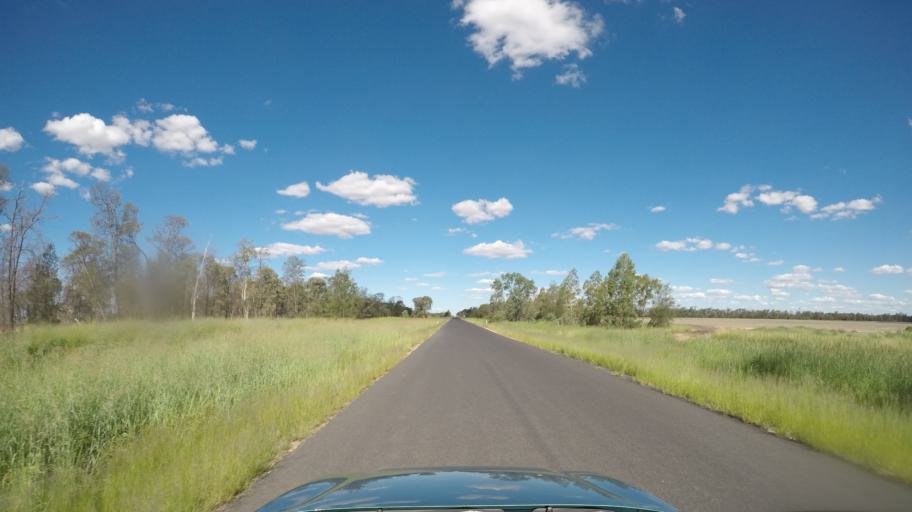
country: AU
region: Queensland
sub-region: Goondiwindi
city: Goondiwindi
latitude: -28.1652
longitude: 150.1716
